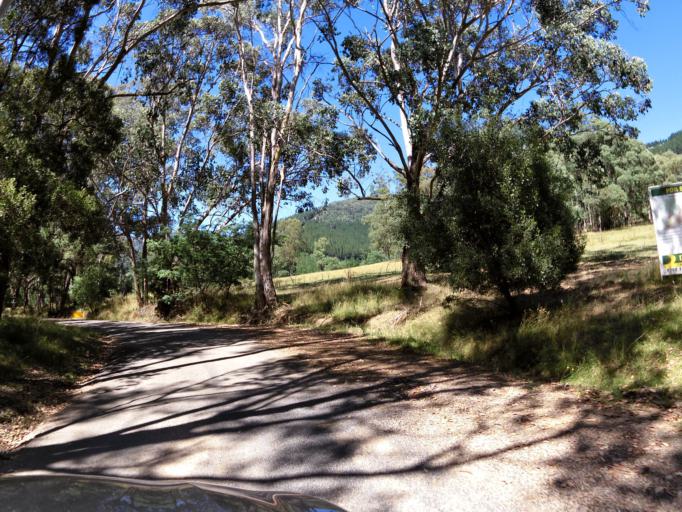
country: AU
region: Victoria
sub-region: Alpine
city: Mount Beauty
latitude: -36.7445
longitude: 146.9543
